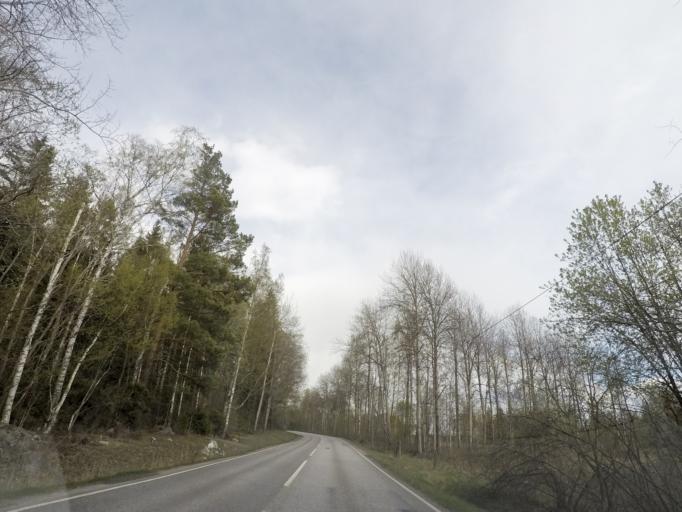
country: SE
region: Vaestmanland
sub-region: Kungsors Kommun
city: Kungsoer
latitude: 59.2854
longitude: 16.1418
